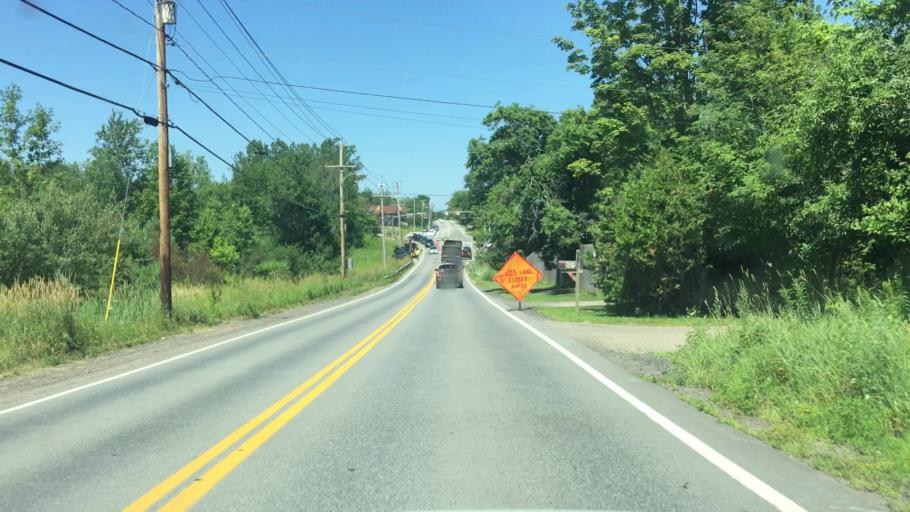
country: US
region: Maine
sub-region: Penobscot County
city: Bangor
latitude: 44.8231
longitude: -68.8072
